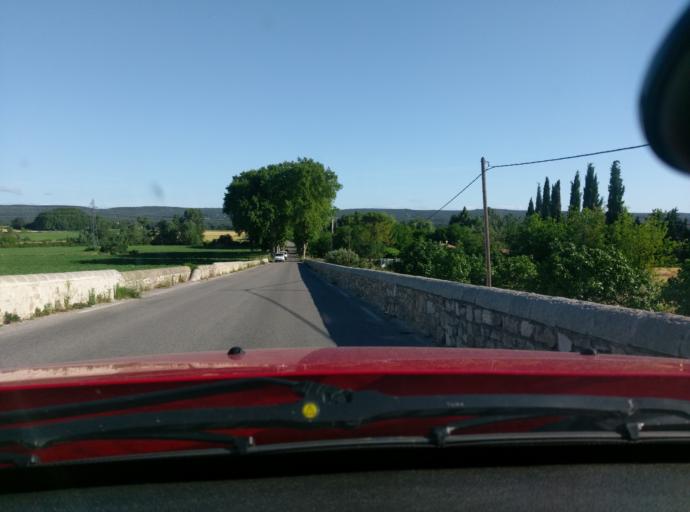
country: FR
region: Languedoc-Roussillon
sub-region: Departement du Gard
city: Uzes
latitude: 44.0303
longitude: 4.4113
